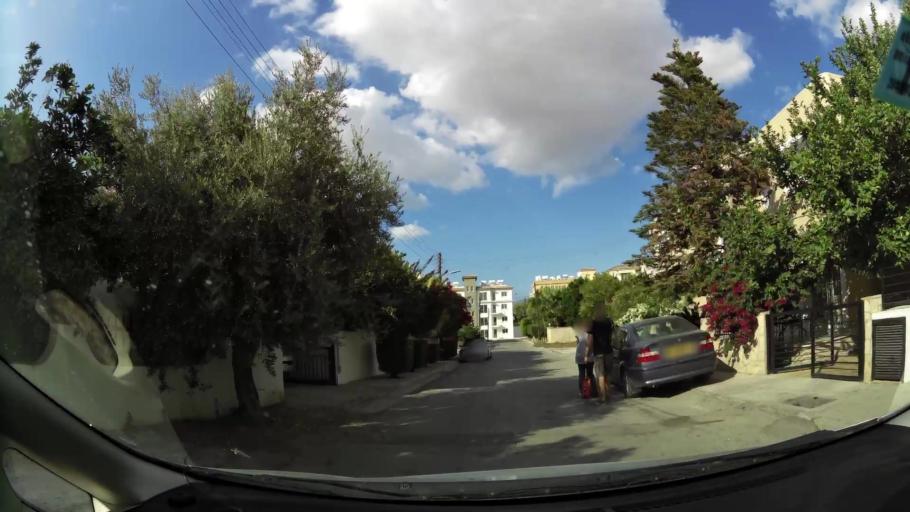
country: CY
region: Lefkosia
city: Nicosia
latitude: 35.1954
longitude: 33.3584
